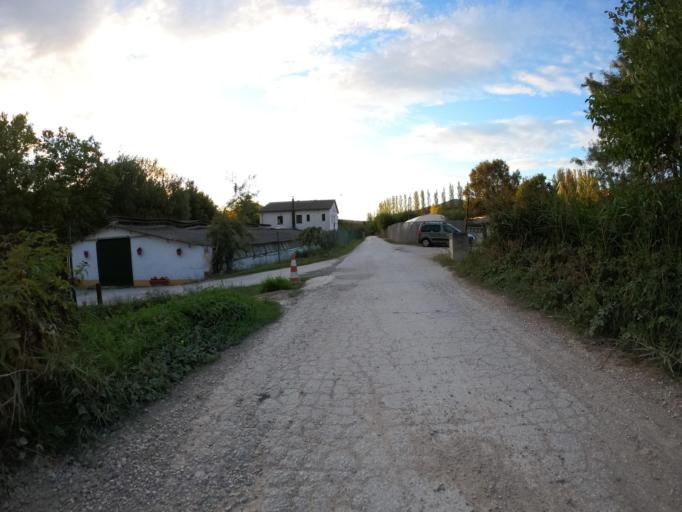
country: ES
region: Navarre
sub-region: Provincia de Navarra
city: Egues-Uharte
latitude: 42.8340
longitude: -1.5783
